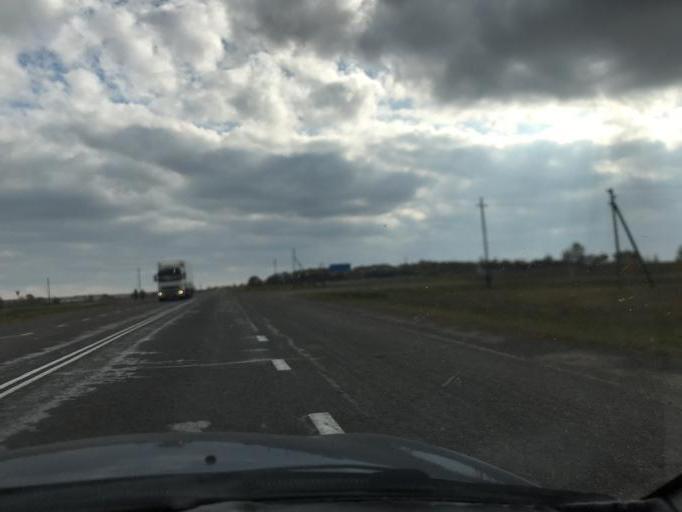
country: BY
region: Grodnenskaya
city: Lida
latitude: 53.7869
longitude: 25.1561
